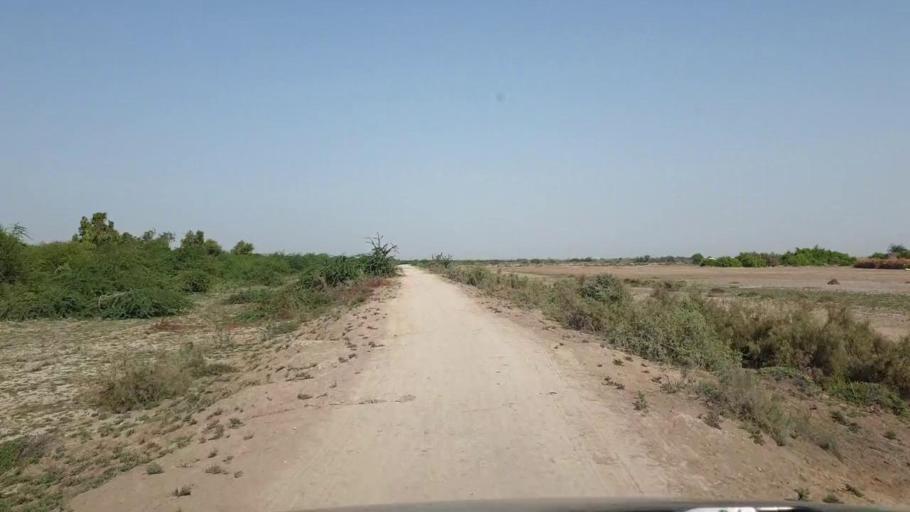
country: PK
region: Sindh
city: Tando Bago
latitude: 24.6495
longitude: 69.0713
